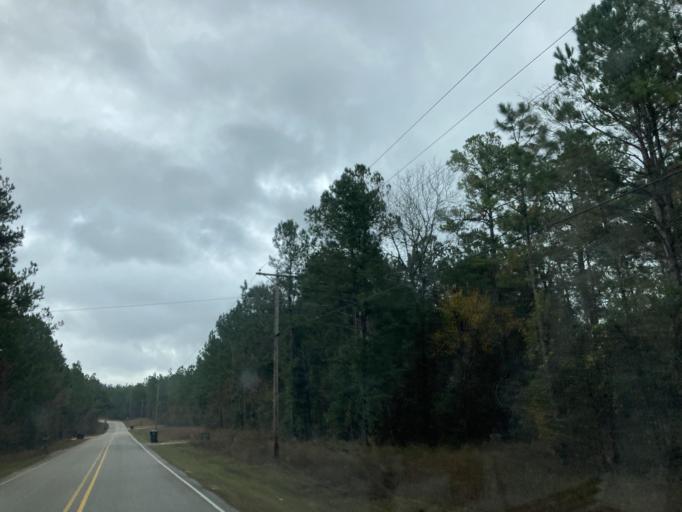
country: US
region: Mississippi
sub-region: Lamar County
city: Lumberton
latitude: 31.1050
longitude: -89.5949
